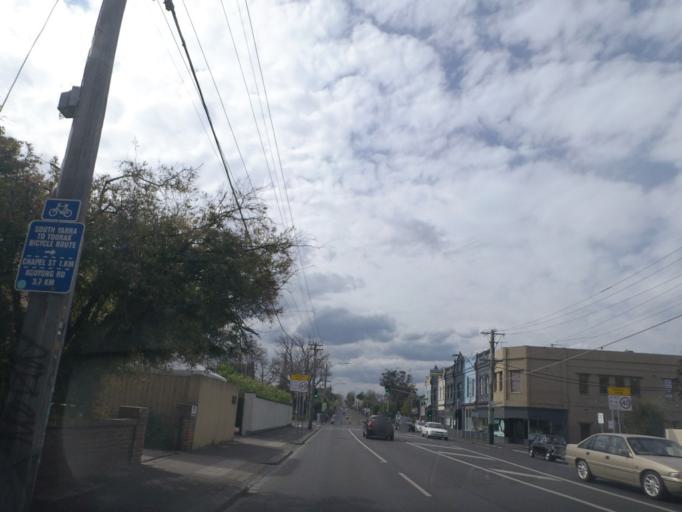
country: AU
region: Victoria
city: Windsor
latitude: -37.8420
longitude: 144.9857
